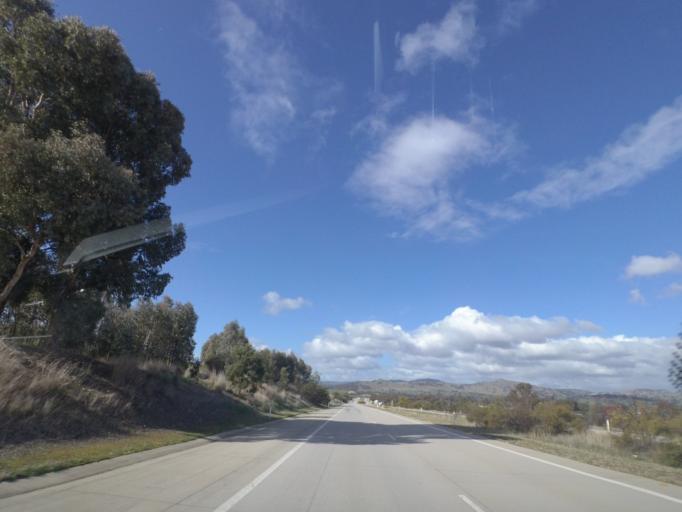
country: AU
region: New South Wales
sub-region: Albury Municipality
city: Lavington
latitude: -35.9154
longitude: 147.1167
